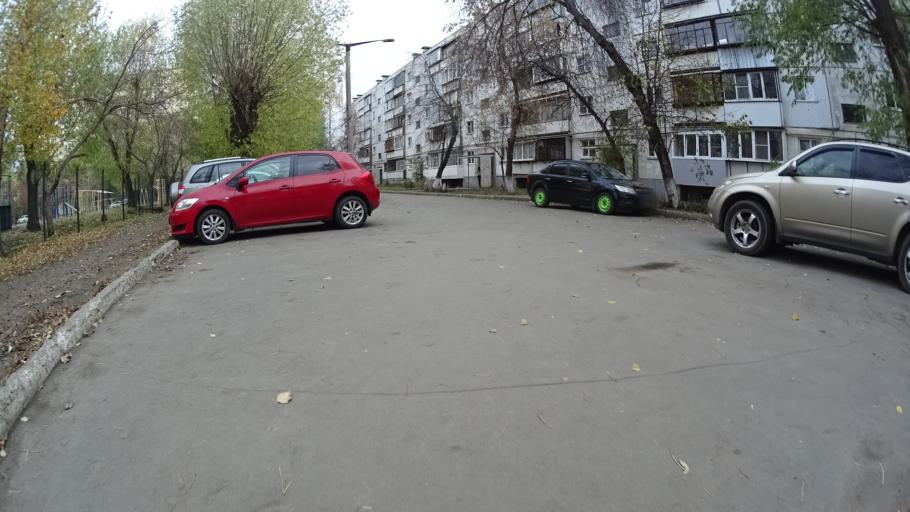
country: RU
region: Chelyabinsk
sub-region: Gorod Chelyabinsk
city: Chelyabinsk
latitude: 55.1915
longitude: 61.3159
